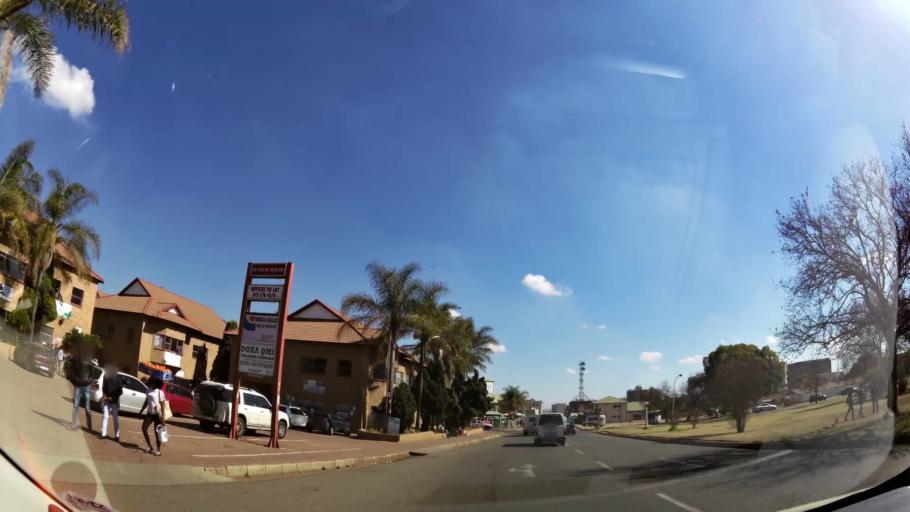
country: ZA
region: Mpumalanga
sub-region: Nkangala District Municipality
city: Witbank
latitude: -25.8764
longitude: 29.2181
